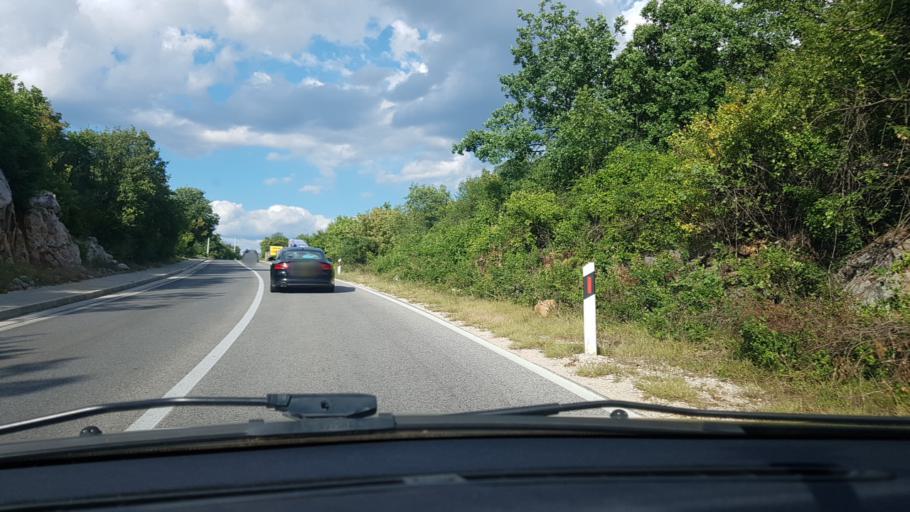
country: HR
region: Splitsko-Dalmatinska
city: Grubine
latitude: 43.4281
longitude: 17.1397
